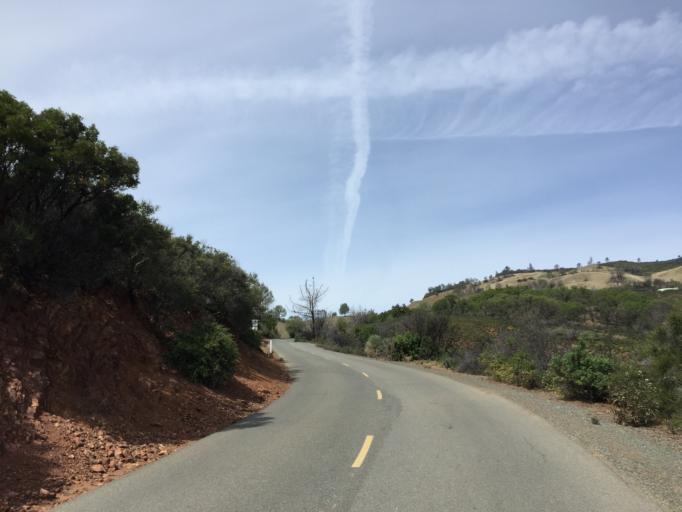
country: US
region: California
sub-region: Contra Costa County
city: Diablo
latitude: 37.8658
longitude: -121.9231
